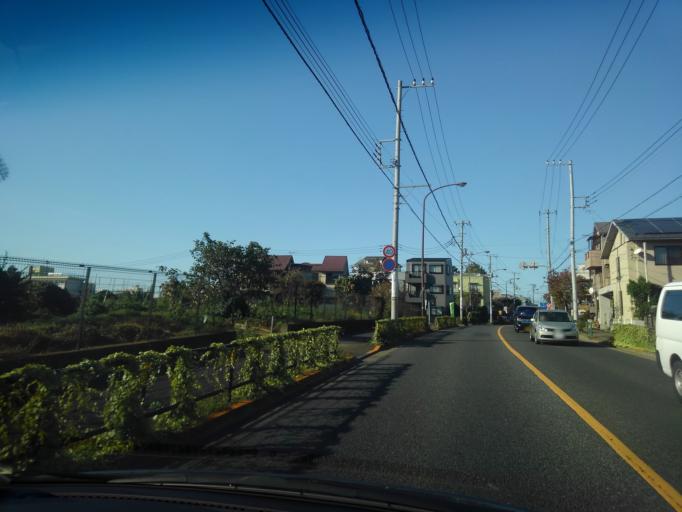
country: JP
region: Tokyo
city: Mitaka-shi
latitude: 35.6792
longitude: 139.5387
